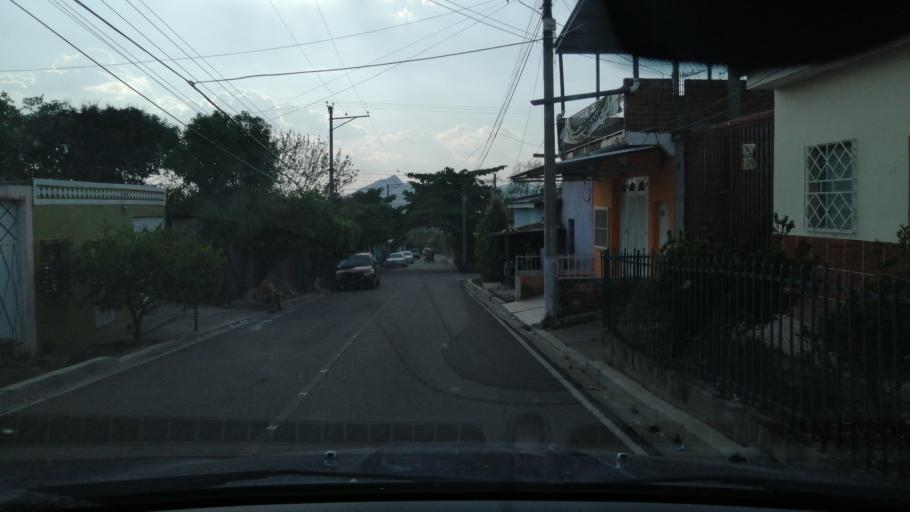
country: SV
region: Santa Ana
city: Metapan
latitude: 14.3326
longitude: -89.4371
